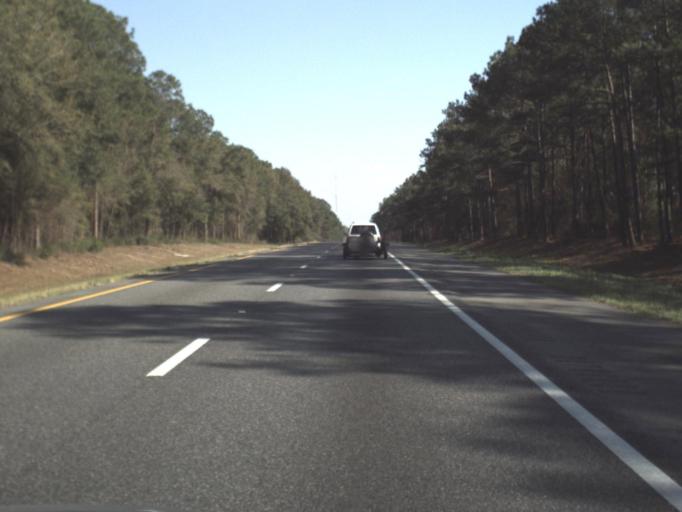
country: US
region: Florida
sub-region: Gadsden County
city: Midway
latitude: 30.5121
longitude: -84.4736
